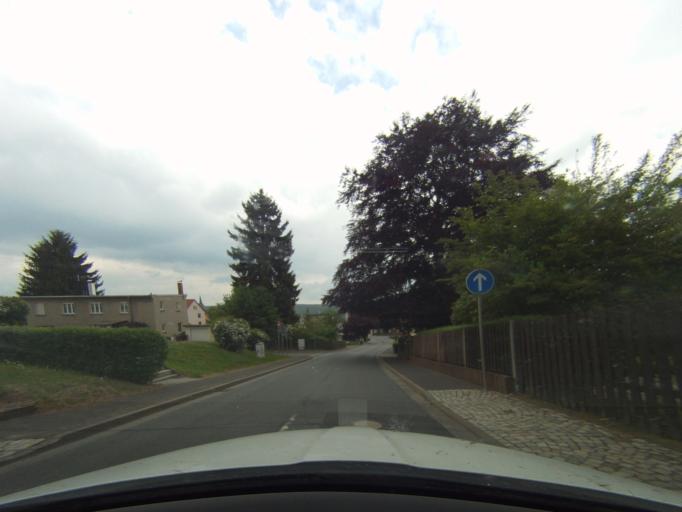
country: DE
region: Thuringia
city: Konigsee
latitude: 50.6583
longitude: 11.0999
